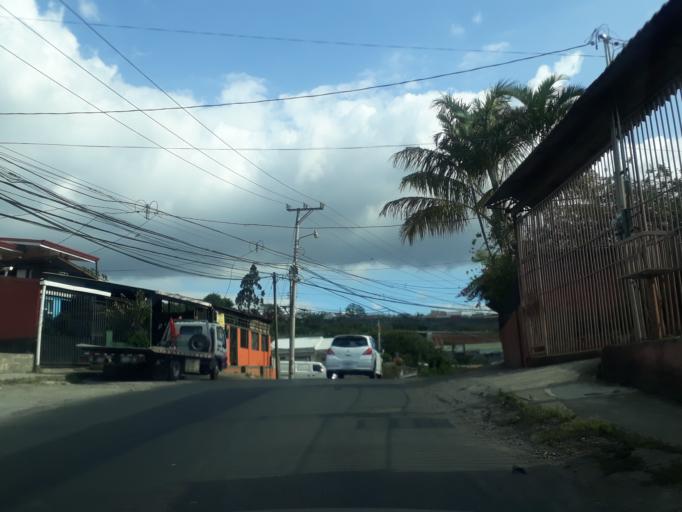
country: CR
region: San Jose
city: Purral
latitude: 9.9767
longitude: -84.0321
